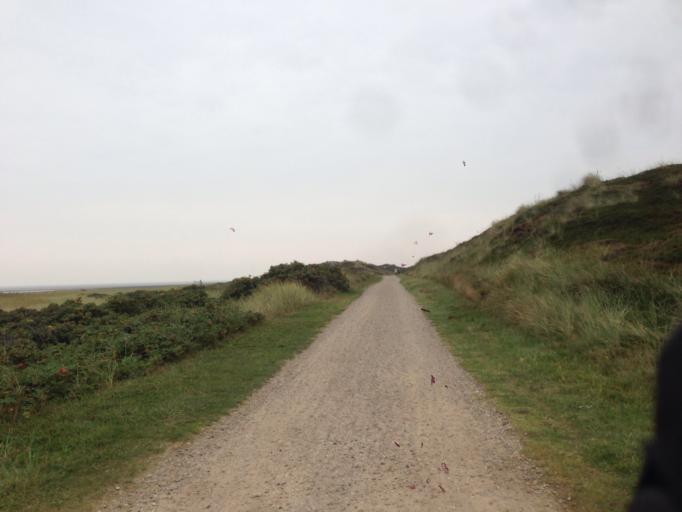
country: DE
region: Schleswig-Holstein
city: Westerland
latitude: 54.8237
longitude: 8.2930
